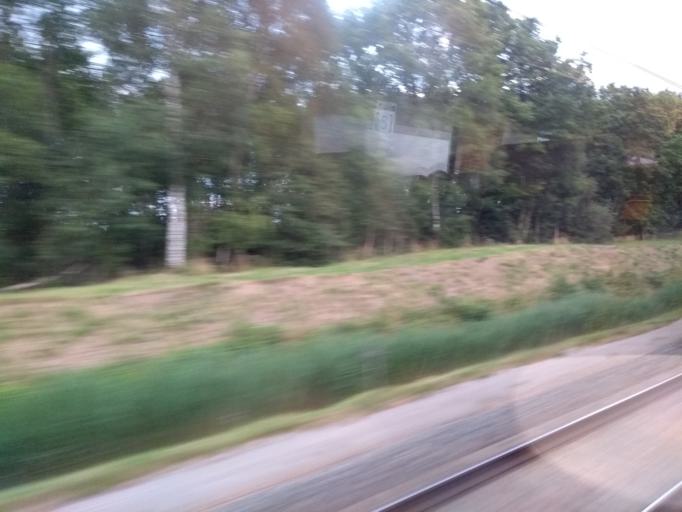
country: NL
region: Overijssel
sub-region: Gemeente Steenwijkerland
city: Steenwijkerwold
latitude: 52.8142
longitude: 6.0784
